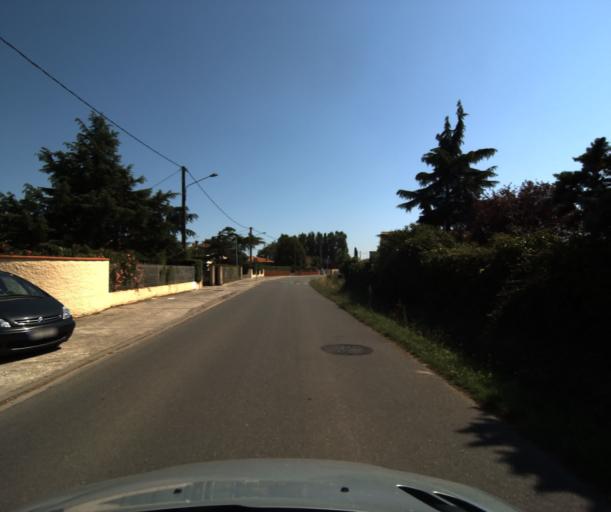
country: FR
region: Midi-Pyrenees
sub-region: Departement de la Haute-Garonne
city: Roquettes
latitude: 43.4737
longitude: 1.3803
